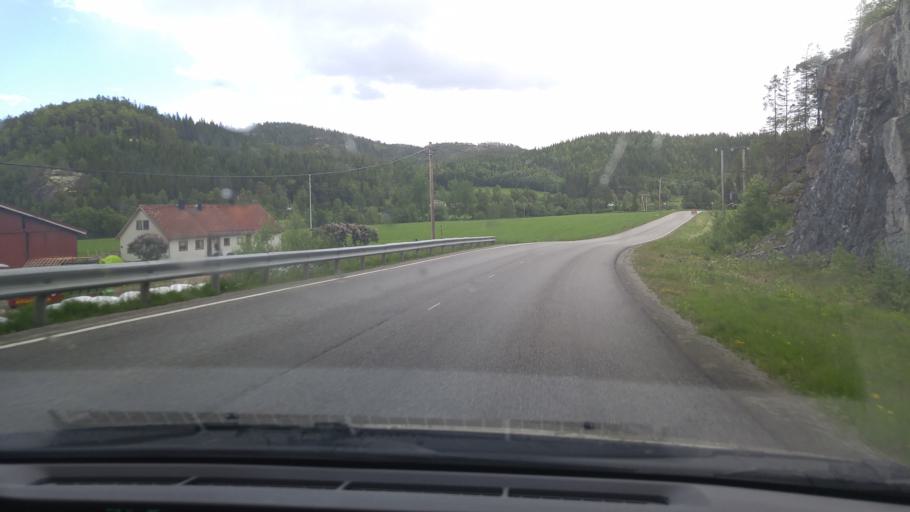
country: NO
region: Nord-Trondelag
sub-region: Namdalseid
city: Namdalseid
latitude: 64.3656
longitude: 11.3201
